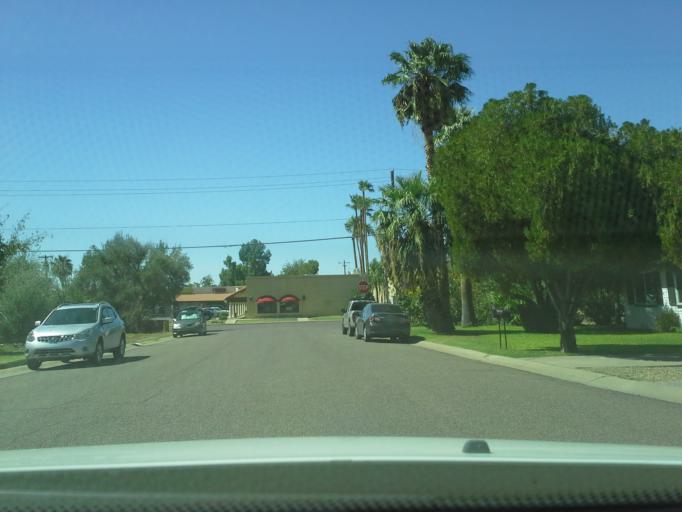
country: US
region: Arizona
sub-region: Maricopa County
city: Phoenix
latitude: 33.5318
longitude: -112.0467
